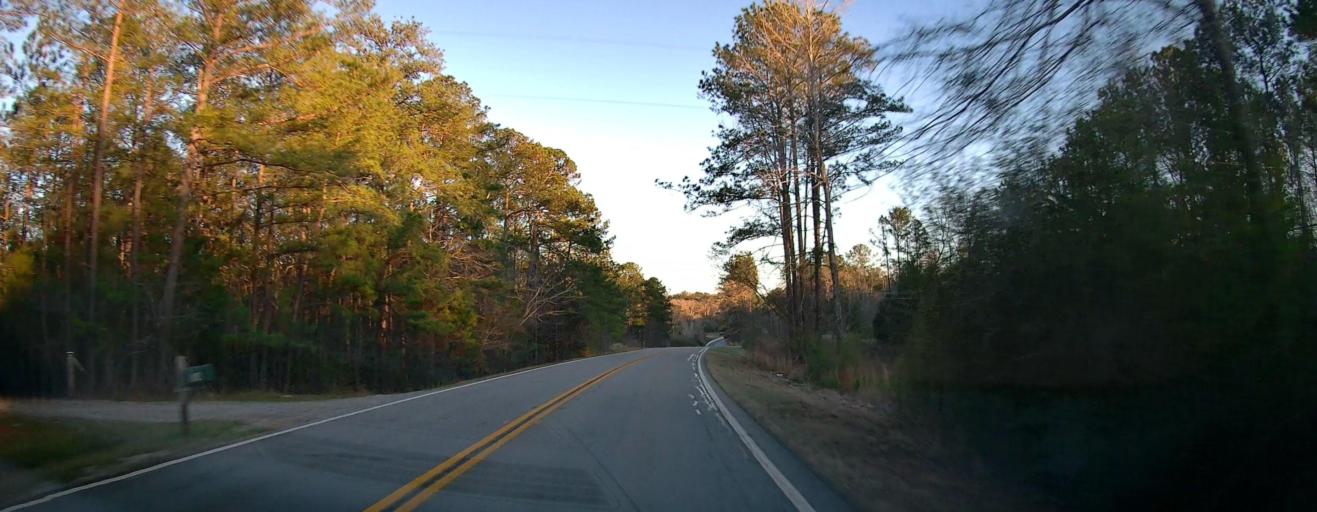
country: US
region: Alabama
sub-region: Lee County
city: Smiths Station
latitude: 32.6208
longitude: -85.0305
